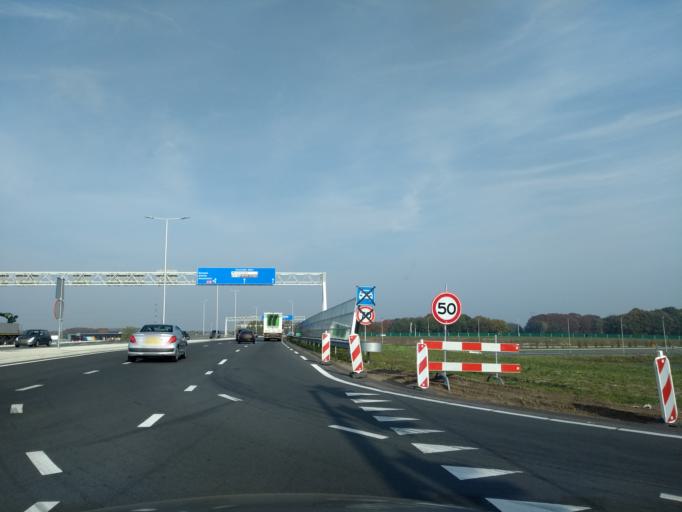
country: NL
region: Overijssel
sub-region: Gemeente Hengelo
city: Hengelo
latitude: 52.2055
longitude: 6.8226
